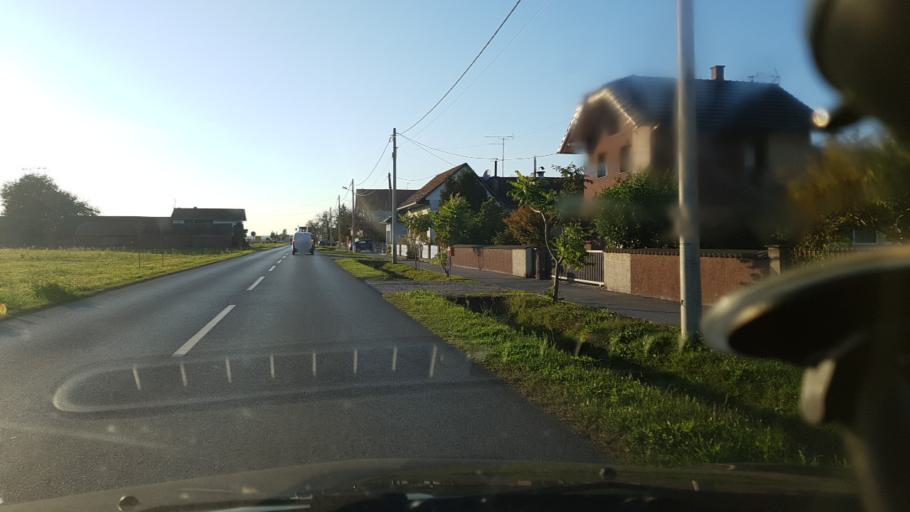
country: HR
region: Koprivnicko-Krizevacka
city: Virje
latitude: 46.0483
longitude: 17.0420
